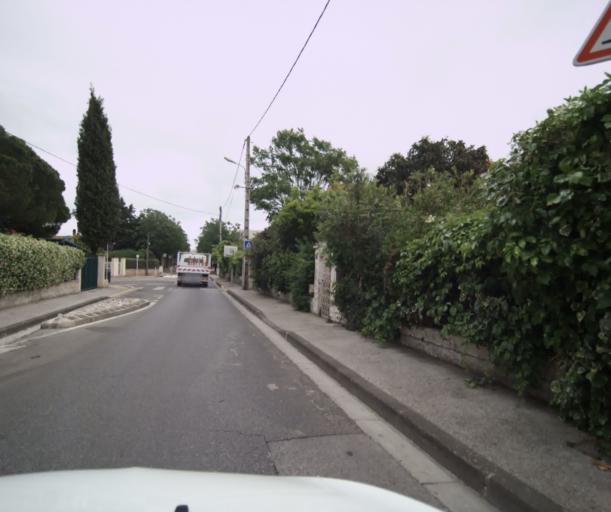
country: FR
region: Provence-Alpes-Cote d'Azur
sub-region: Departement du Var
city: La Valette-du-Var
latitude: 43.1270
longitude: 5.9688
